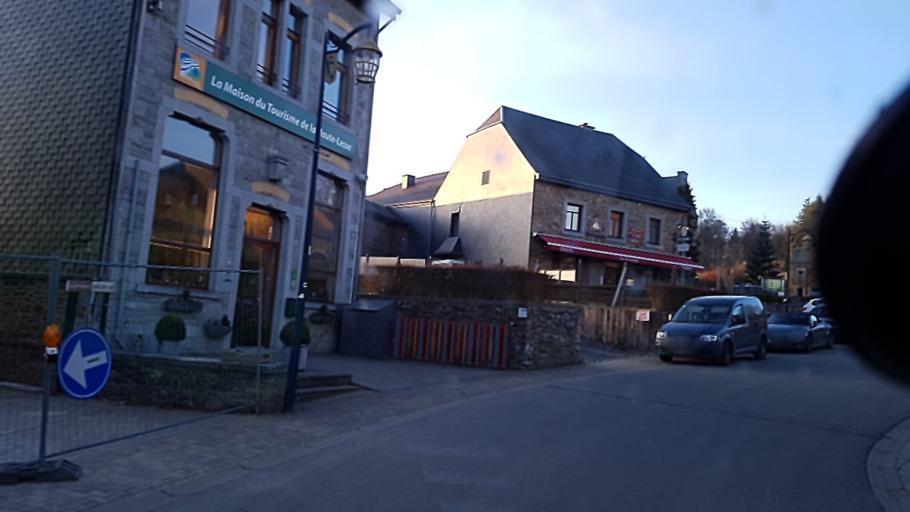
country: BE
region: Wallonia
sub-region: Province du Luxembourg
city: Daverdisse
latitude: 50.0071
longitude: 5.1600
